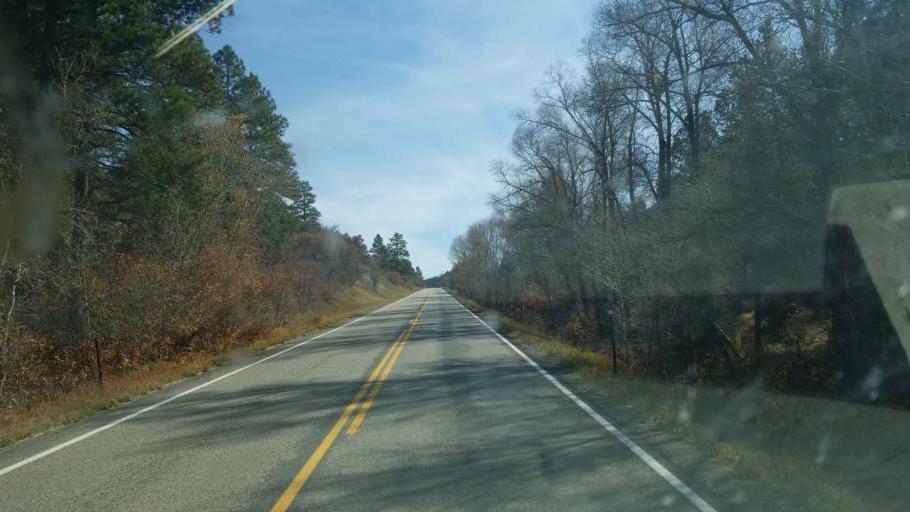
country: US
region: New Mexico
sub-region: Rio Arriba County
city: Dulce
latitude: 37.0796
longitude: -106.8601
